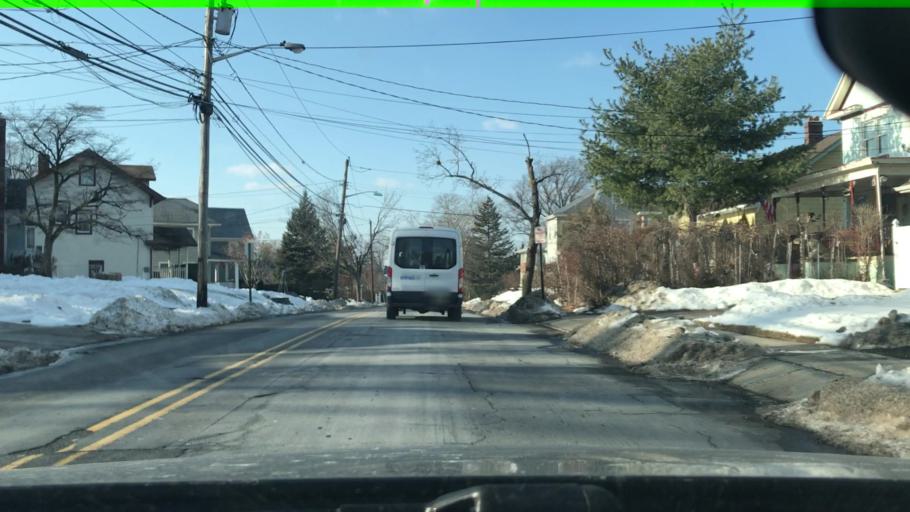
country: US
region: New Jersey
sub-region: Union County
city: Union
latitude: 40.6952
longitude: -74.2742
